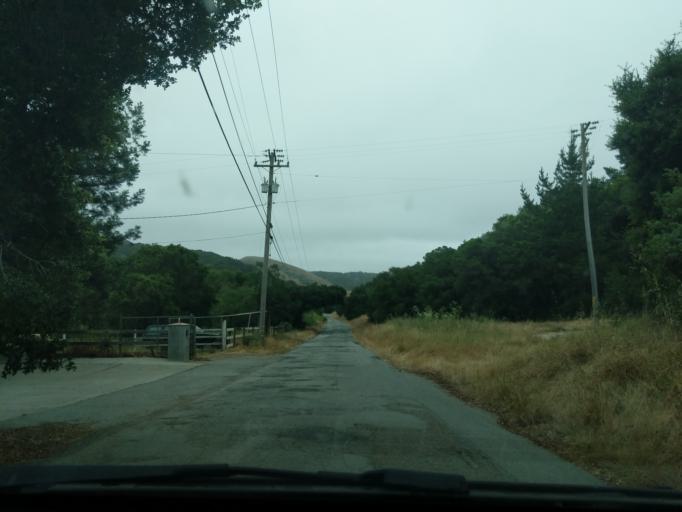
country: US
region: California
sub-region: San Benito County
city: Aromas
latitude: 36.8745
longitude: -121.6215
